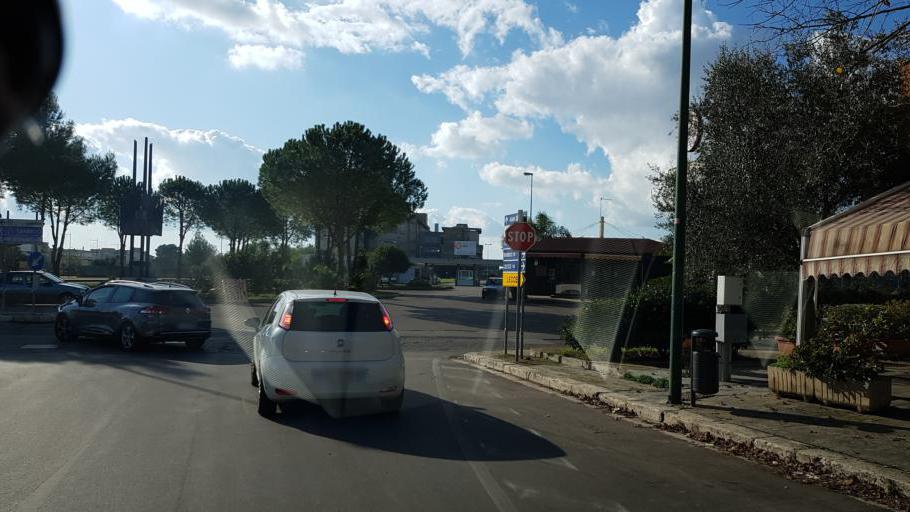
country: IT
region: Apulia
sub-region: Provincia di Lecce
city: Campi Salentina
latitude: 40.4038
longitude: 18.0158
